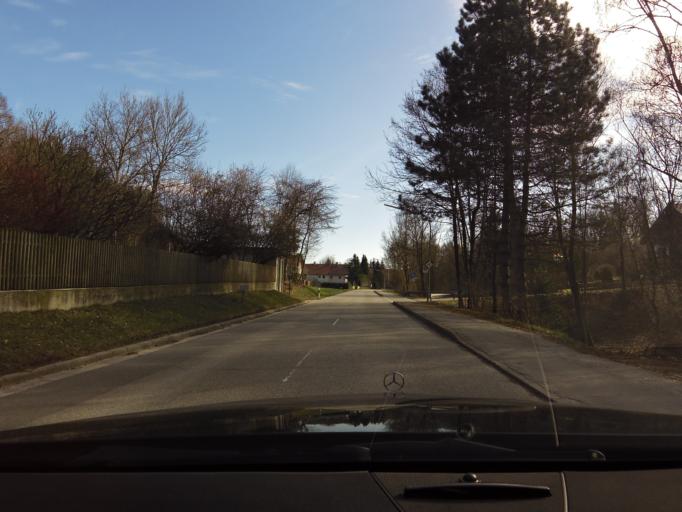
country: DE
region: Bavaria
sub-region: Lower Bavaria
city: Tiefenbach
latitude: 48.5065
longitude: 12.0988
